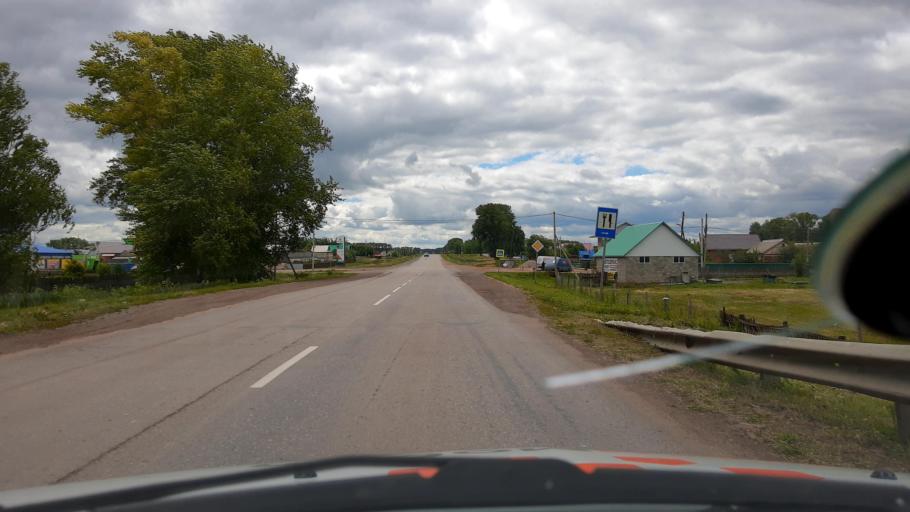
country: RU
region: Bashkortostan
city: Buzdyak
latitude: 54.6888
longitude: 54.5561
